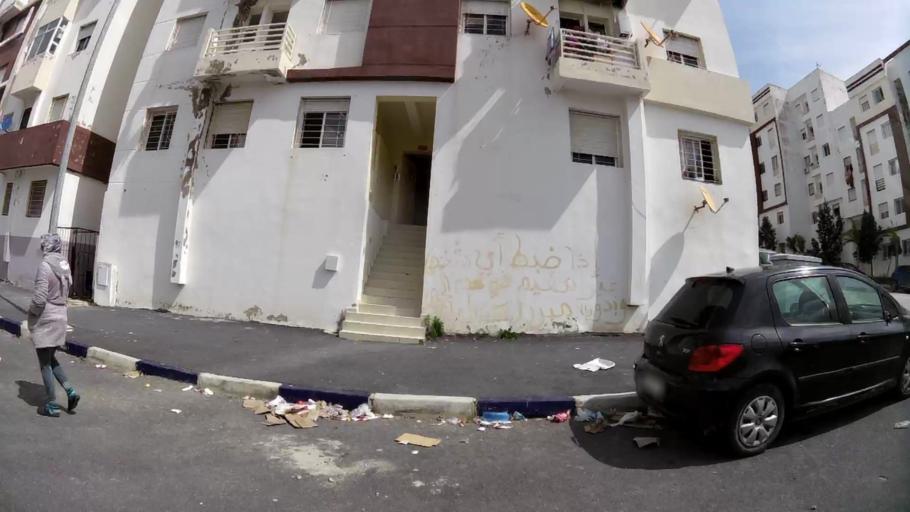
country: MA
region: Tanger-Tetouan
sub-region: Tanger-Assilah
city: Tangier
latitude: 35.7607
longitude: -5.7628
